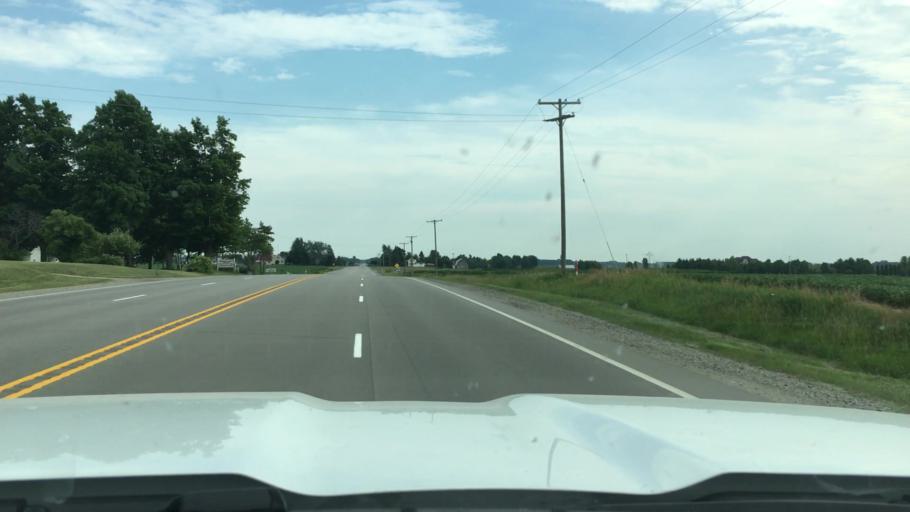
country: US
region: Michigan
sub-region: Sanilac County
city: Marlette
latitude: 43.3810
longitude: -83.0860
